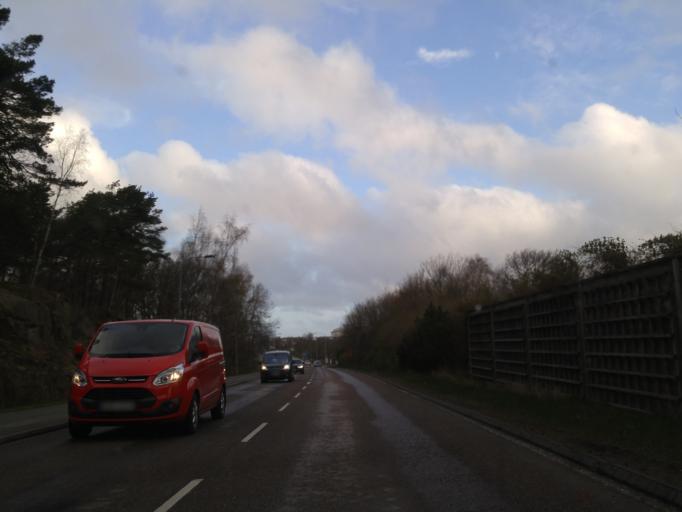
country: SE
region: Vaestra Goetaland
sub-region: Goteborg
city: Majorna
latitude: 57.6699
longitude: 11.8867
